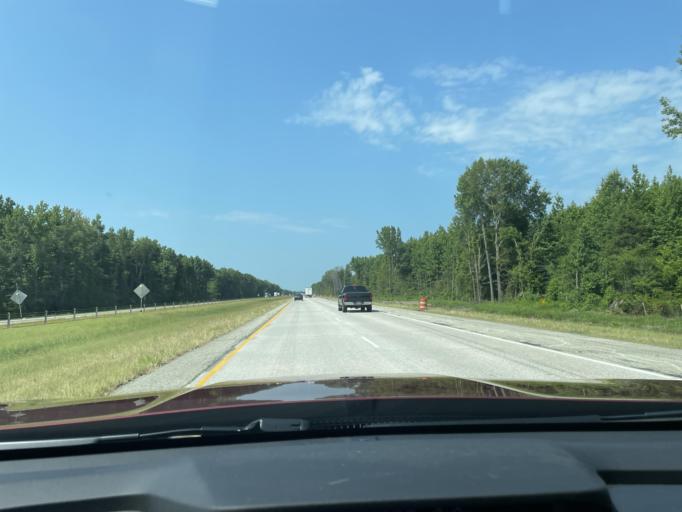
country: US
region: Arkansas
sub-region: White County
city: Searcy
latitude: 35.1656
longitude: -91.7757
